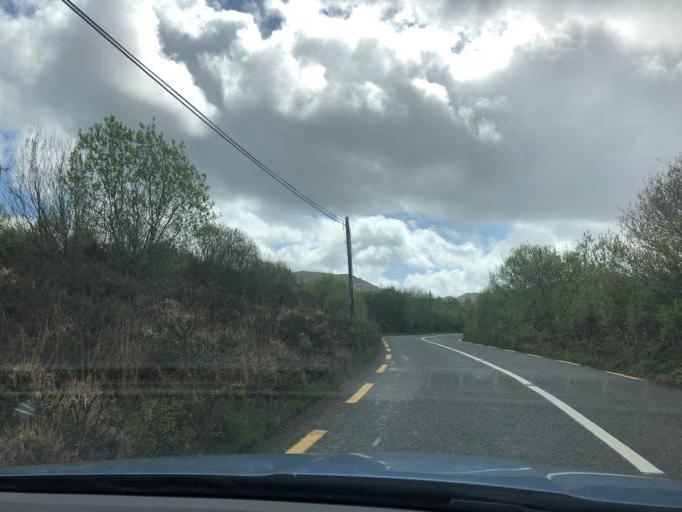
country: IE
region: Munster
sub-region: Ciarrai
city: Killorglin
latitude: 51.8369
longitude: -9.9169
